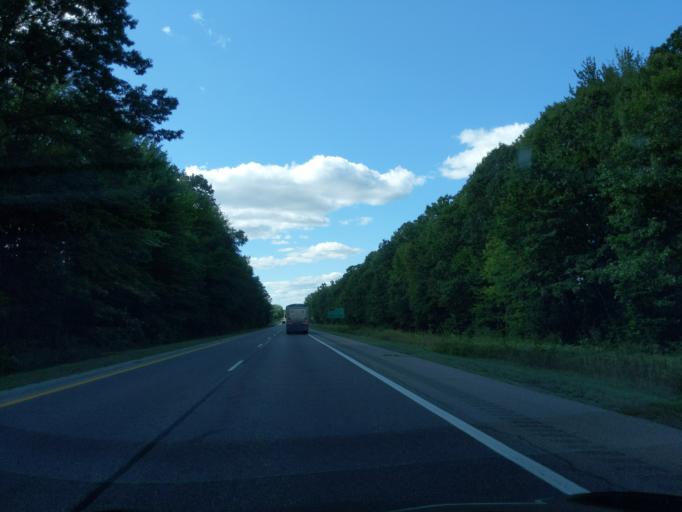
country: US
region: Michigan
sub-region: Muskegon County
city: Fruitport
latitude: 43.1248
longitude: -86.1366
